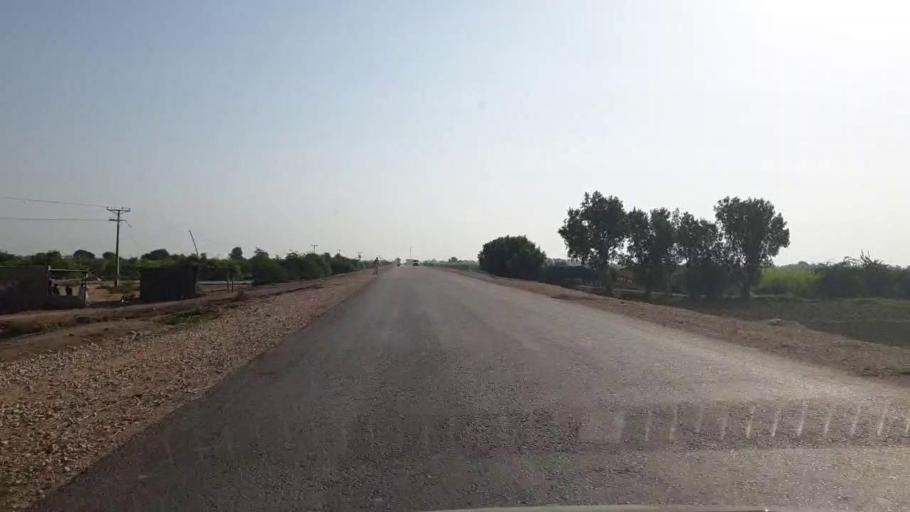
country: PK
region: Sindh
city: Badin
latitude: 24.6589
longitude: 68.9311
